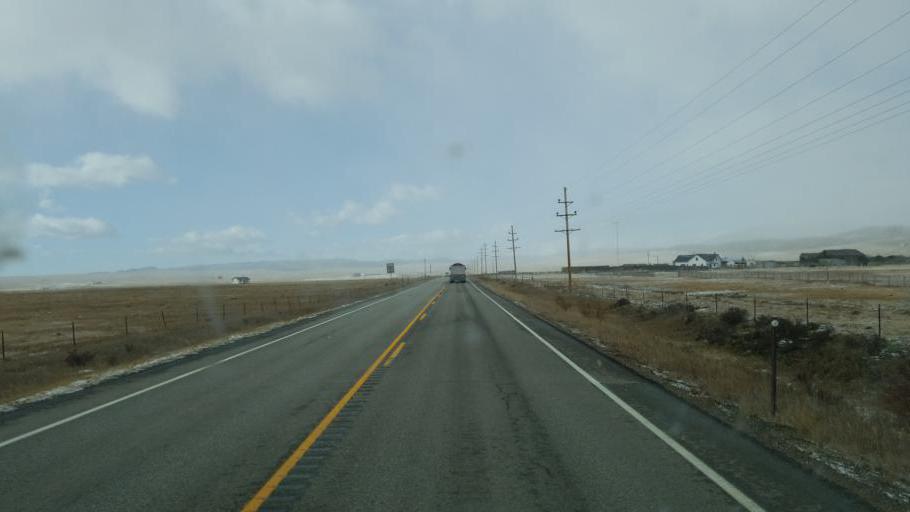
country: US
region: Colorado
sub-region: Park County
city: Fairplay
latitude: 39.3741
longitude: -105.8042
